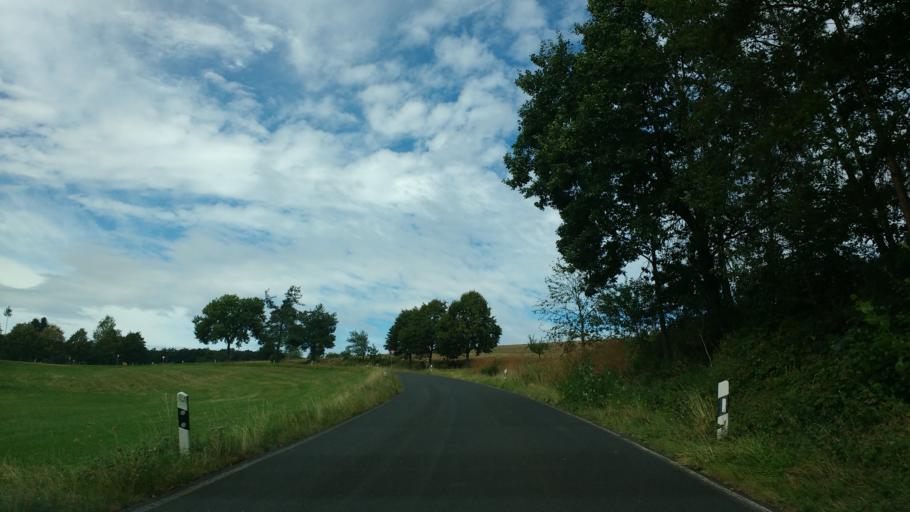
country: DE
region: Bavaria
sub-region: Regierungsbezirk Unterfranken
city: Geiselwind
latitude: 49.7943
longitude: 10.5155
